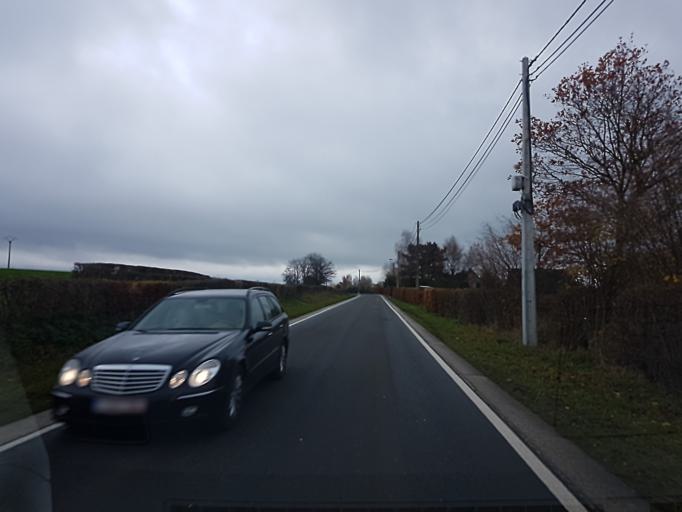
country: BE
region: Wallonia
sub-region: Province de Liege
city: Jalhay
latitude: 50.5706
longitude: 5.9689
